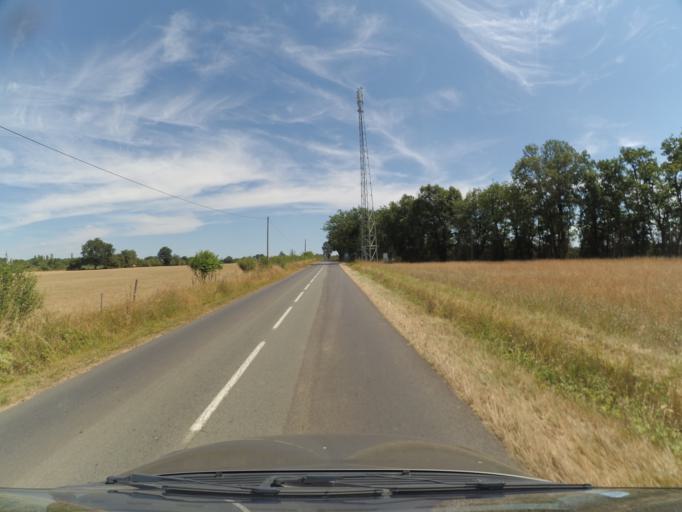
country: FR
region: Poitou-Charentes
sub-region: Departement de la Vienne
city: La Villedieu-du-Clain
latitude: 46.4091
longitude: 0.3369
